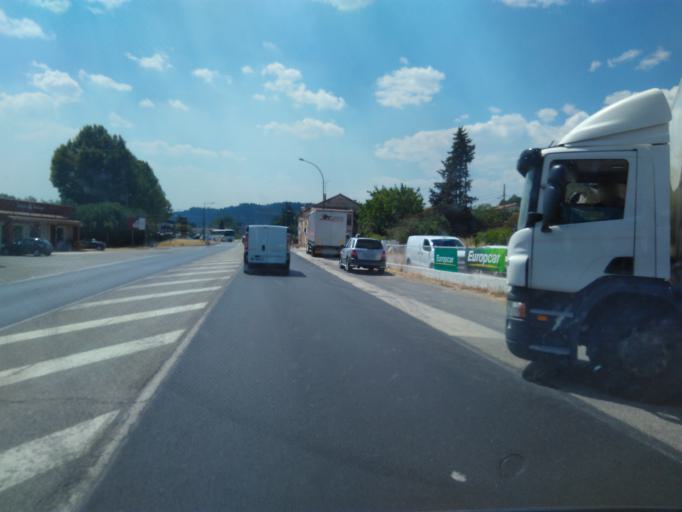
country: FR
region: Provence-Alpes-Cote d'Azur
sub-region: Departement du Var
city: Le Luc
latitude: 43.3939
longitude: 6.3251
